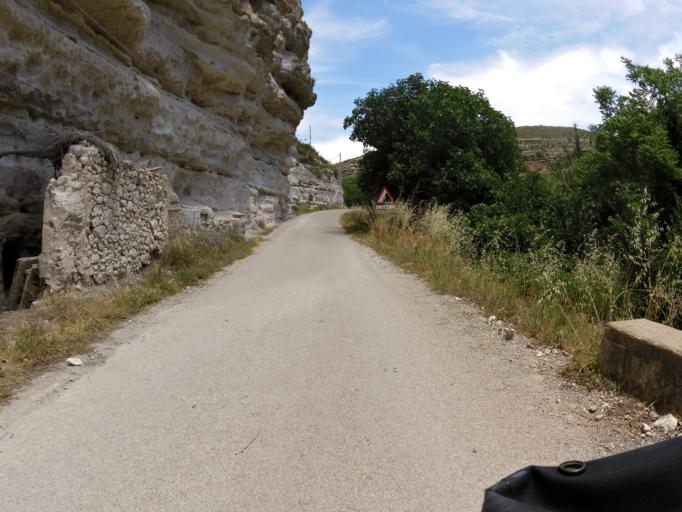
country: ES
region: Castille-La Mancha
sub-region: Provincia de Albacete
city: Jorquera
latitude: 39.1587
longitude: -1.5688
